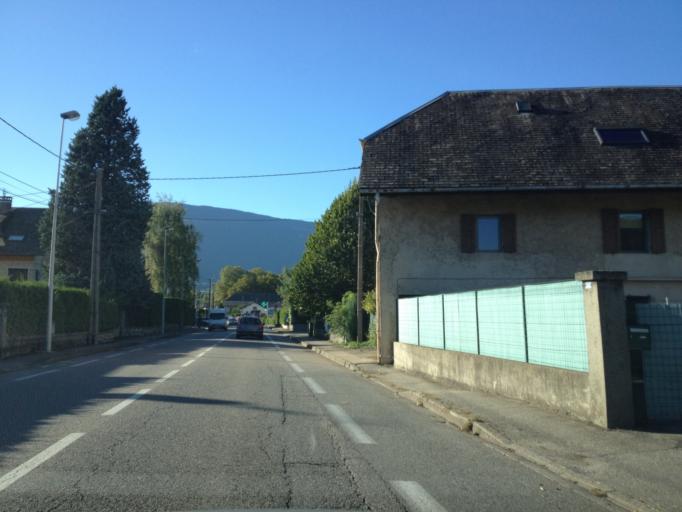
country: FR
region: Rhone-Alpes
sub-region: Departement de la Savoie
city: Cognin
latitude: 45.5795
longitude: 5.8932
